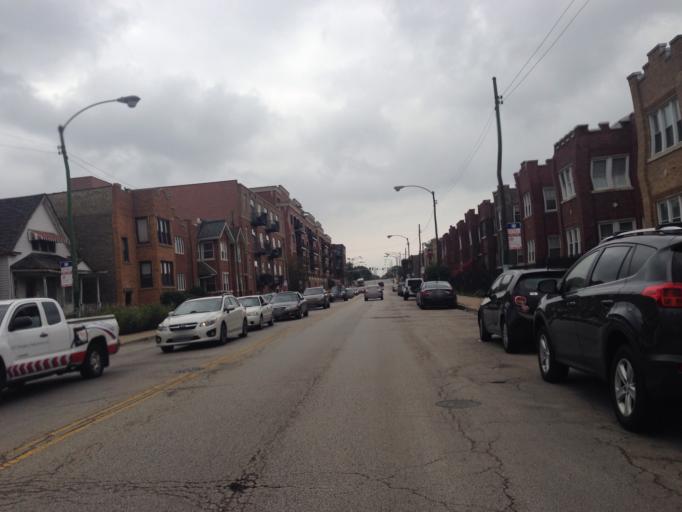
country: US
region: Illinois
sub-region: Cook County
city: Lincolnwood
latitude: 41.9322
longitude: -87.6870
